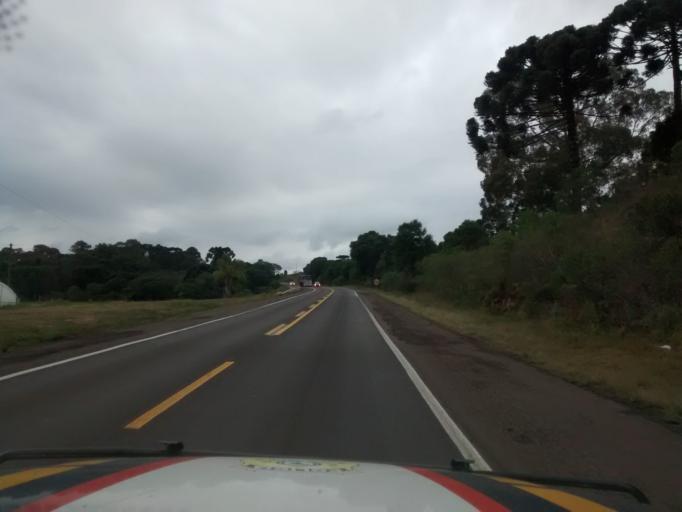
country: BR
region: Rio Grande do Sul
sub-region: Lagoa Vermelha
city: Lagoa Vermelha
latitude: -28.2277
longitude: -51.6191
